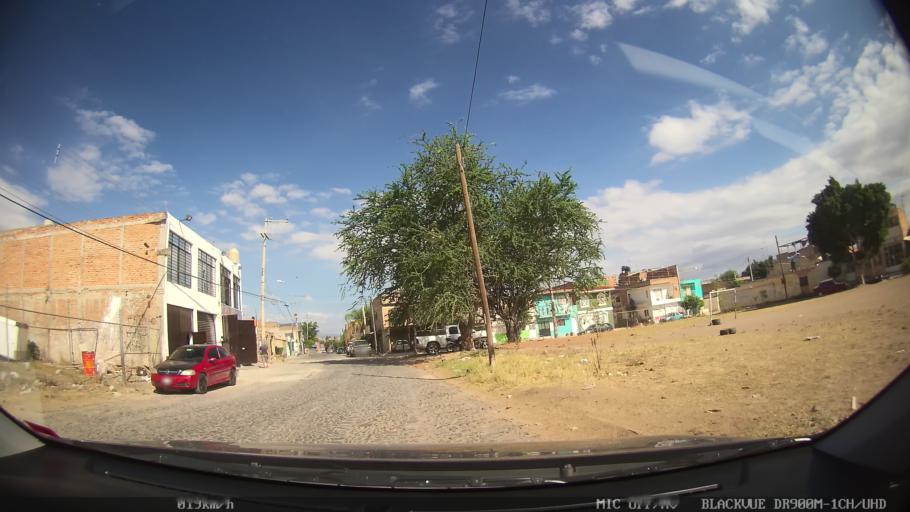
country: MX
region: Jalisco
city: Tonala
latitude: 20.6501
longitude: -103.2500
